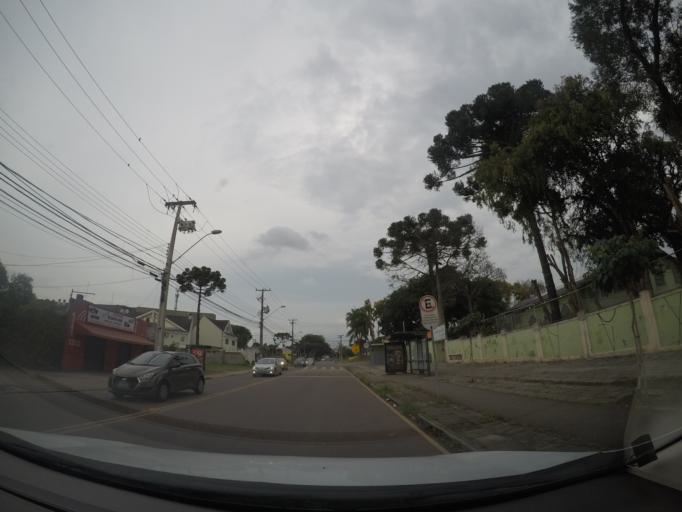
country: BR
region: Parana
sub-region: Curitiba
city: Curitiba
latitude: -25.4629
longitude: -49.2463
